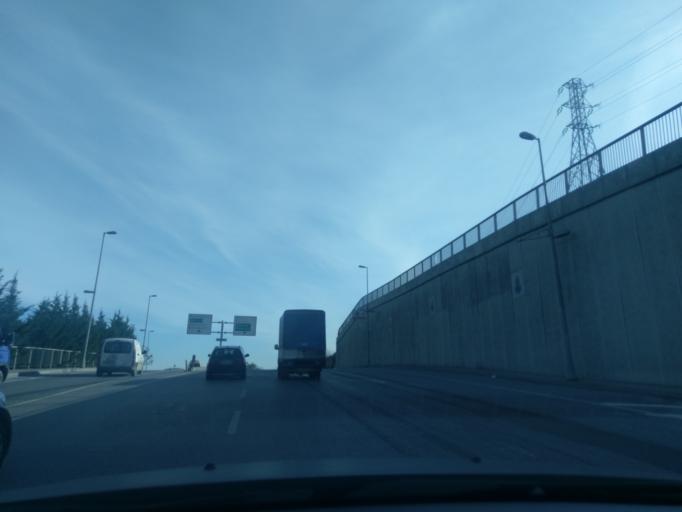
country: TR
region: Istanbul
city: Basaksehir
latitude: 41.0604
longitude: 28.7531
